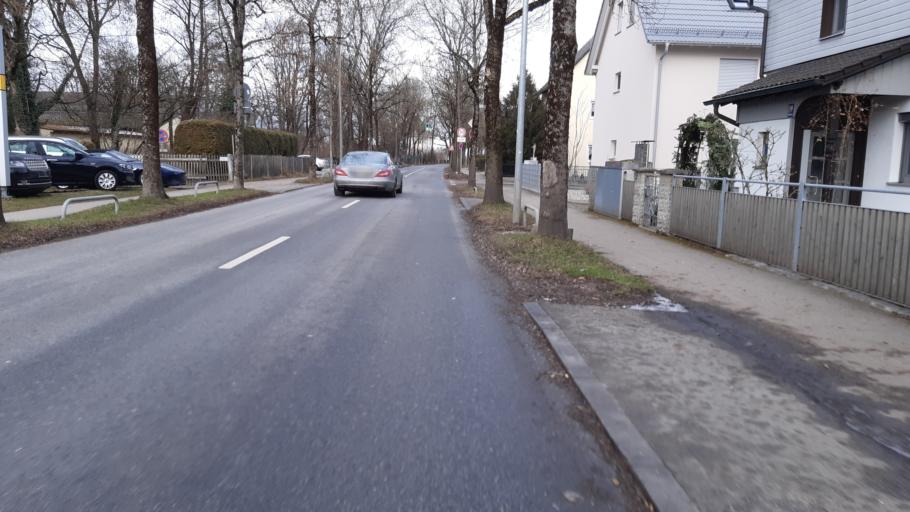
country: DE
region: Bavaria
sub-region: Upper Bavaria
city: Karlsfeld
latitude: 48.1996
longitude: 11.5244
